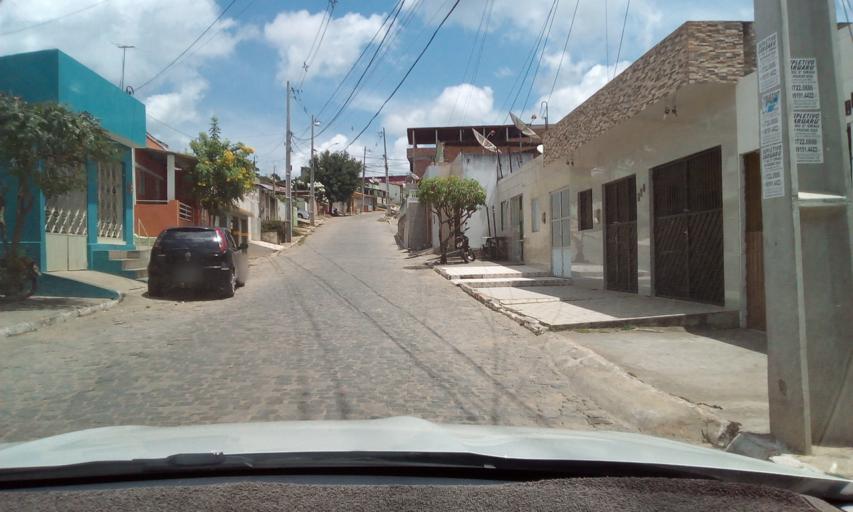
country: BR
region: Pernambuco
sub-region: Bonito
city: Bonito
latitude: -8.4772
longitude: -35.7291
